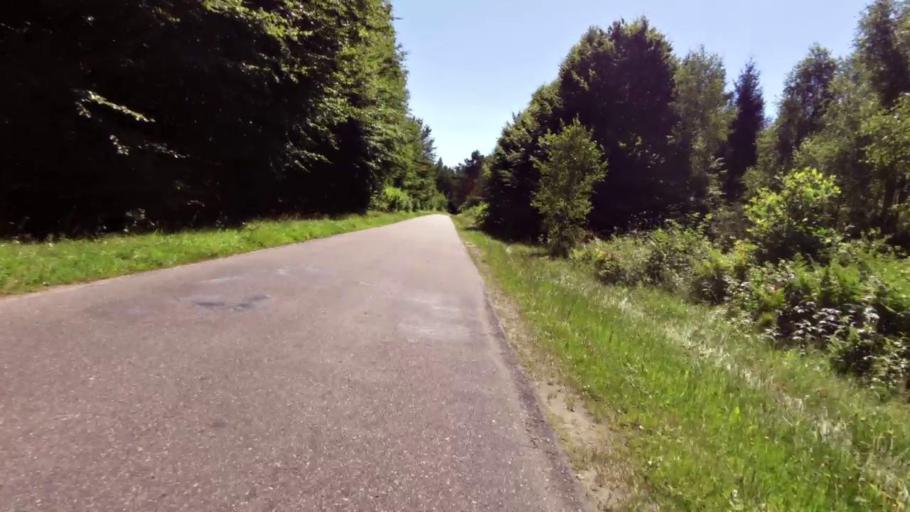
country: PL
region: West Pomeranian Voivodeship
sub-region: Powiat szczecinecki
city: Bialy Bor
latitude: 53.9414
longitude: 16.8535
